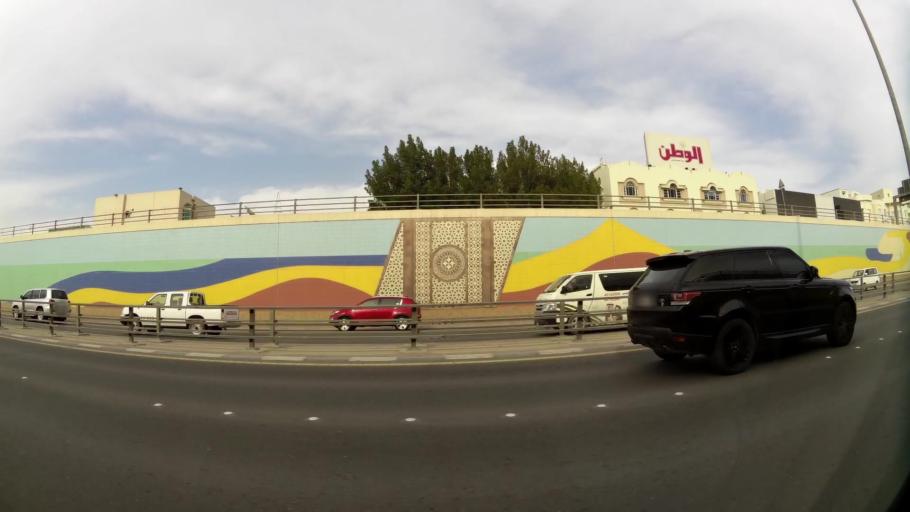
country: QA
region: Baladiyat ad Dawhah
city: Doha
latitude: 25.2622
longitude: 51.4981
